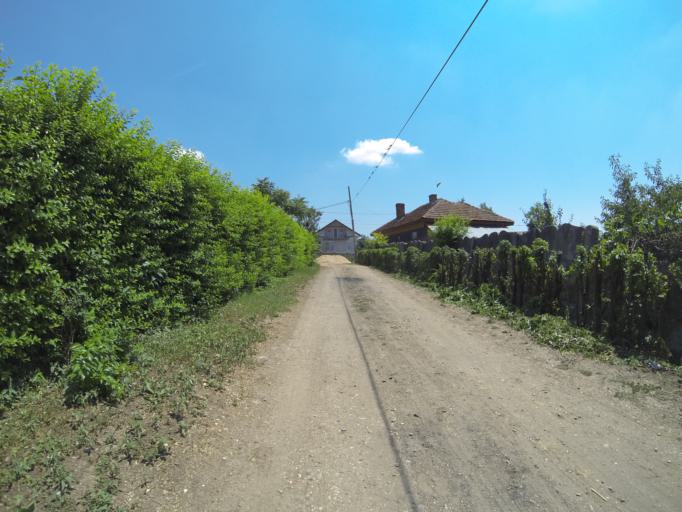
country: RO
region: Dolj
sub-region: Comuna Segarcea
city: Segarcea
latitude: 44.0886
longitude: 23.7533
